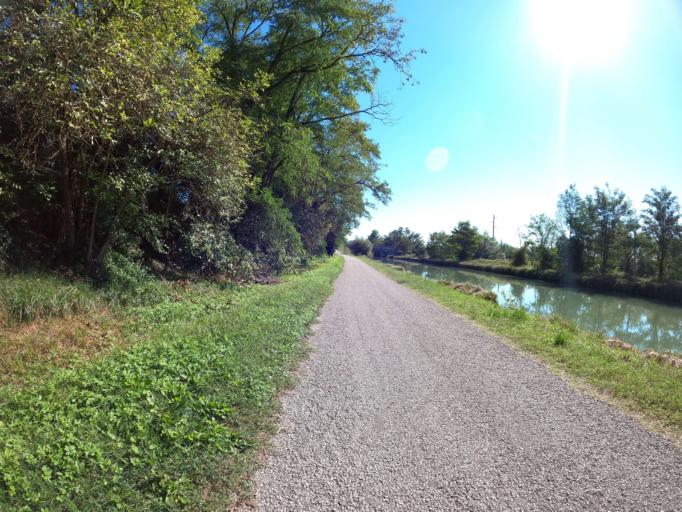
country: FR
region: Aquitaine
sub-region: Departement du Lot-et-Garonne
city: Castelculier
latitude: 44.1712
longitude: 0.6835
